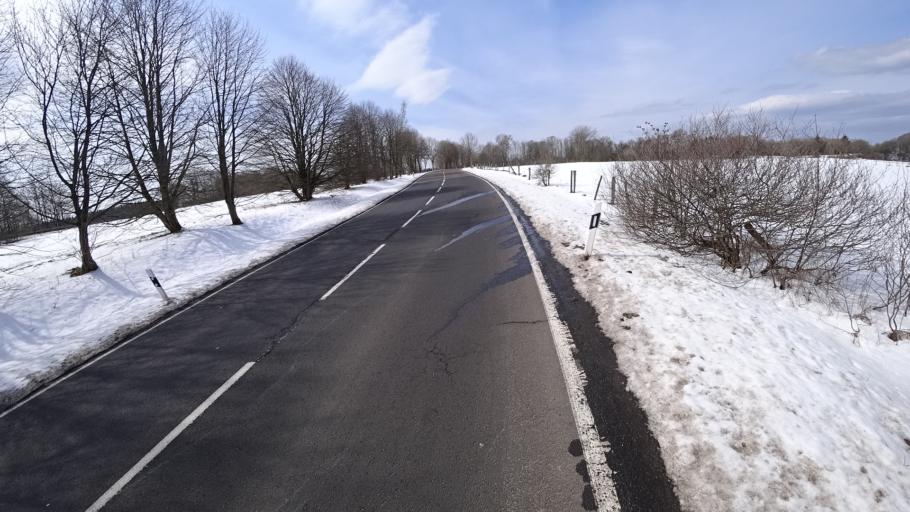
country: DE
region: Rheinland-Pfalz
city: Kausen
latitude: 50.7218
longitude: 7.8676
